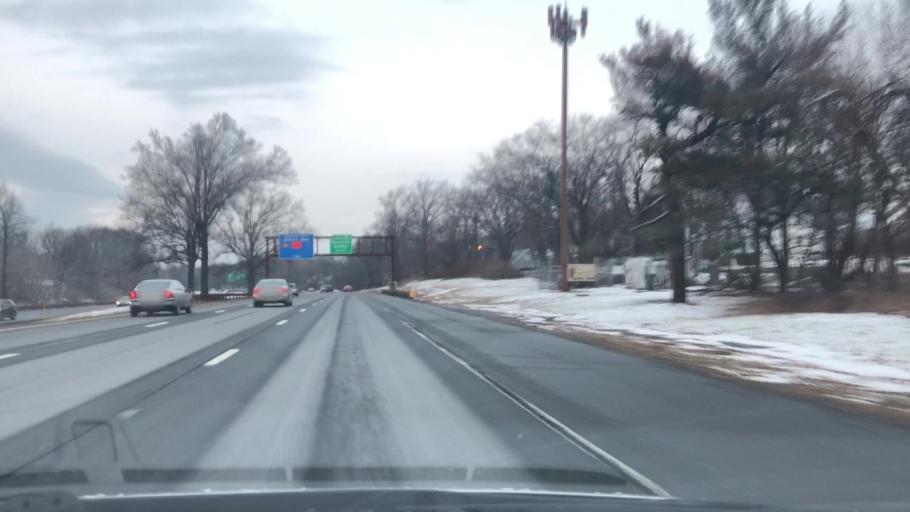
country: US
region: New Jersey
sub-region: Essex County
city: Brookdale
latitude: 40.8206
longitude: -74.1776
